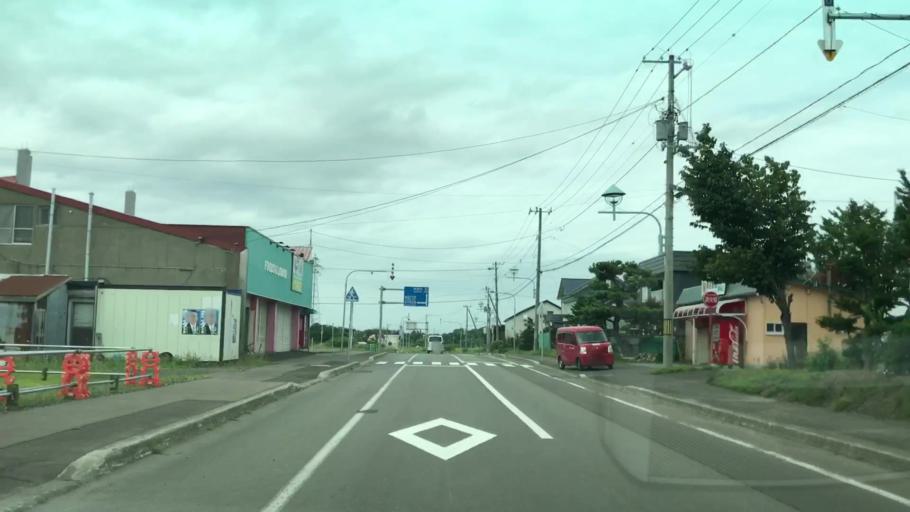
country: JP
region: Hokkaido
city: Iwanai
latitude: 42.9846
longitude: 140.6148
